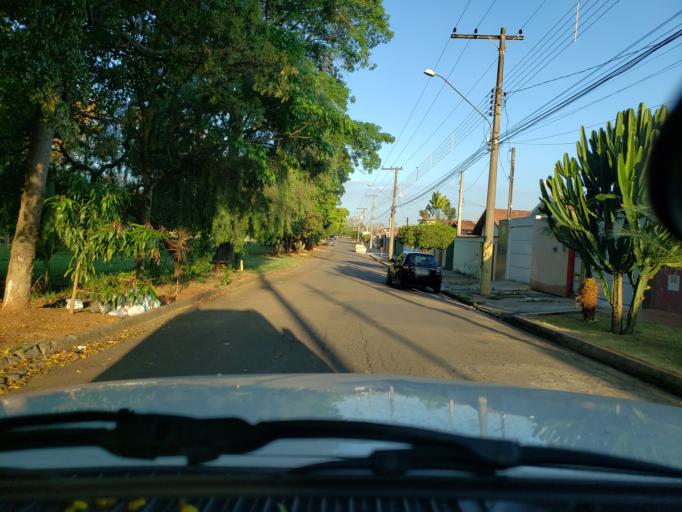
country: BR
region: Sao Paulo
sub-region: Moji-Guacu
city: Mogi-Gaucu
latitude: -22.3409
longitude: -46.9384
